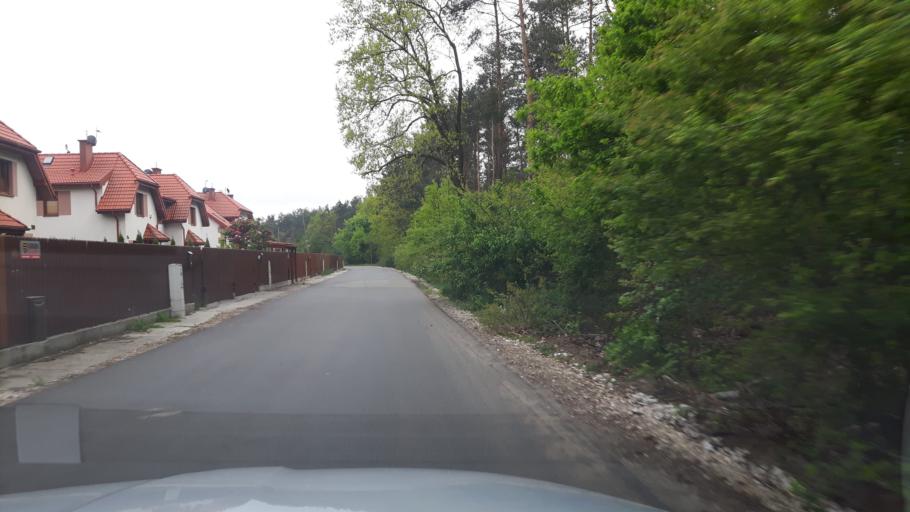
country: PL
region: Masovian Voivodeship
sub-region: Warszawa
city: Rembertow
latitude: 52.2780
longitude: 21.1476
